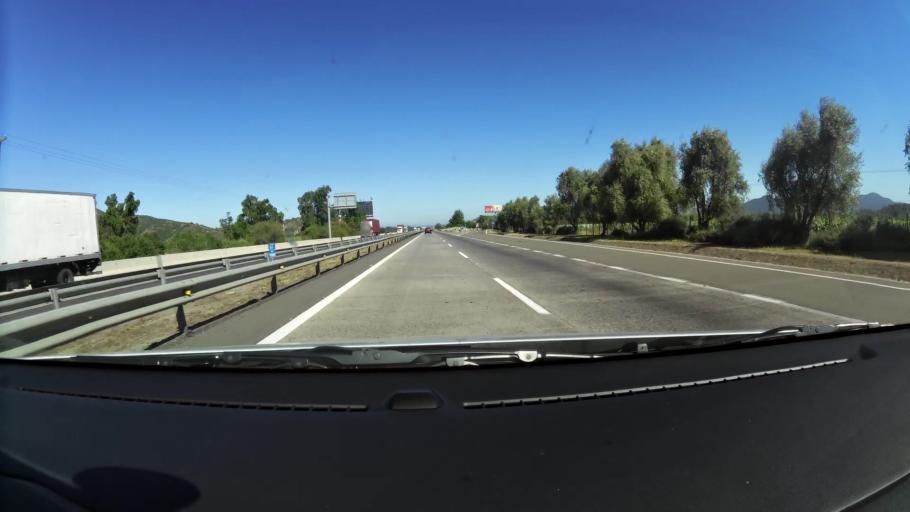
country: CL
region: Valparaiso
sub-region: Provincia de Marga Marga
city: Villa Alemana
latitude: -33.3629
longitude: -71.3167
